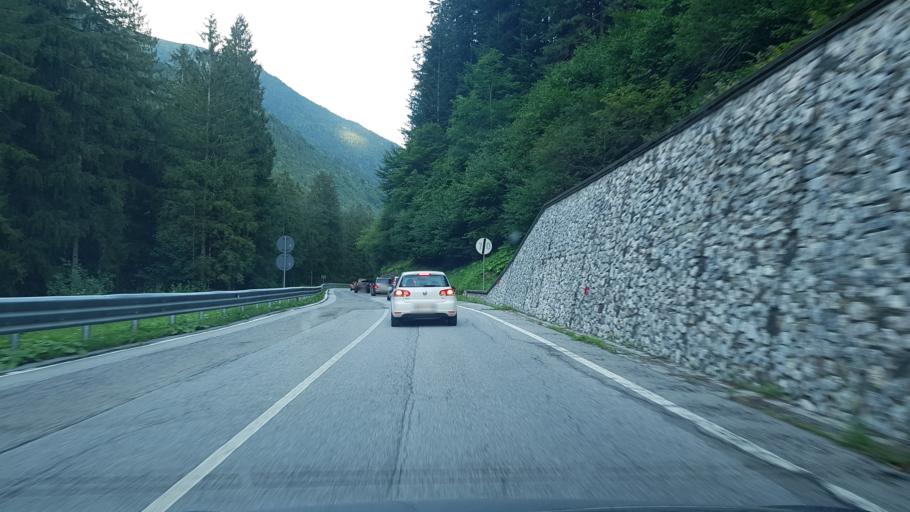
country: IT
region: Friuli Venezia Giulia
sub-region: Provincia di Udine
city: Rigolato
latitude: 46.5662
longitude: 12.8359
